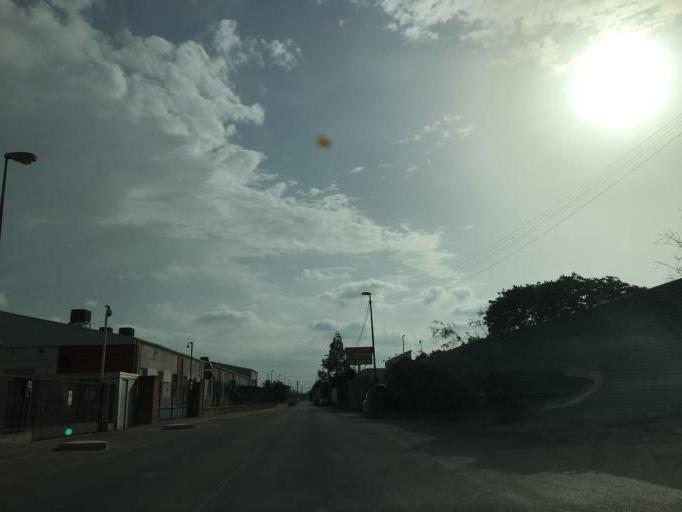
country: ES
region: Murcia
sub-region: Murcia
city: Murcia
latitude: 38.0136
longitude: -1.1034
